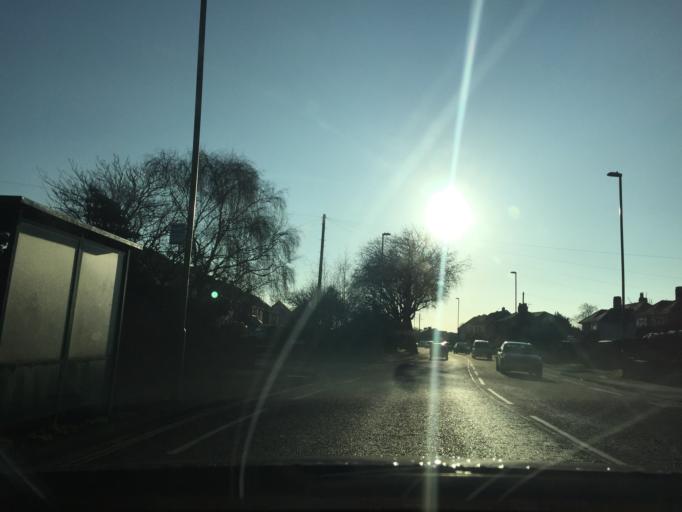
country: GB
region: England
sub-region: Hampshire
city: Gosport
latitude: 50.7942
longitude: -1.1623
